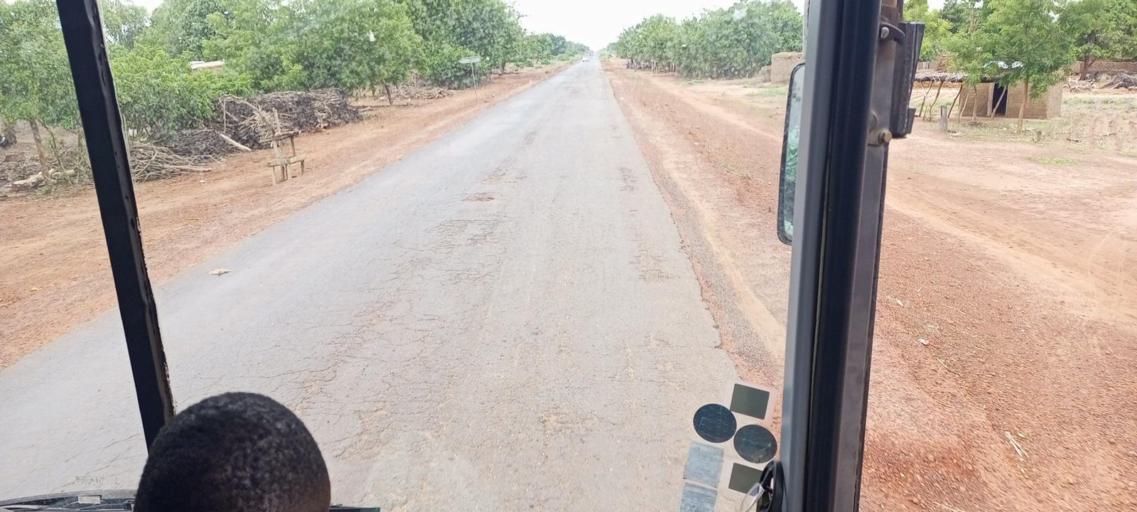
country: ML
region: Sikasso
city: Koutiala
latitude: 12.5788
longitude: -5.6091
